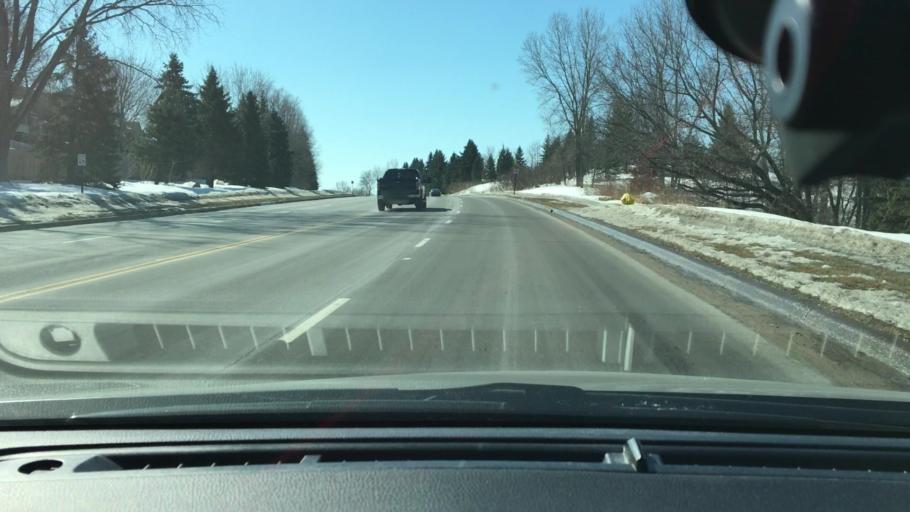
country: US
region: Minnesota
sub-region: Hennepin County
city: Maple Grove
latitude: 45.0577
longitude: -93.4455
